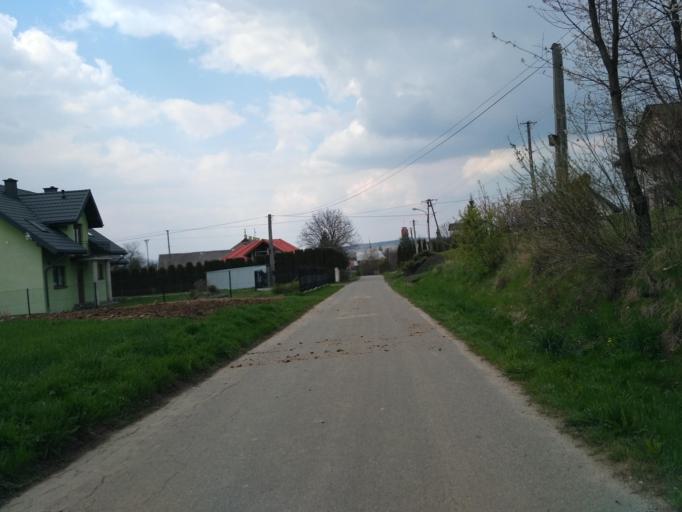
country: PL
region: Subcarpathian Voivodeship
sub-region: Powiat brzozowski
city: Gorki
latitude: 49.6445
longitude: 22.0446
